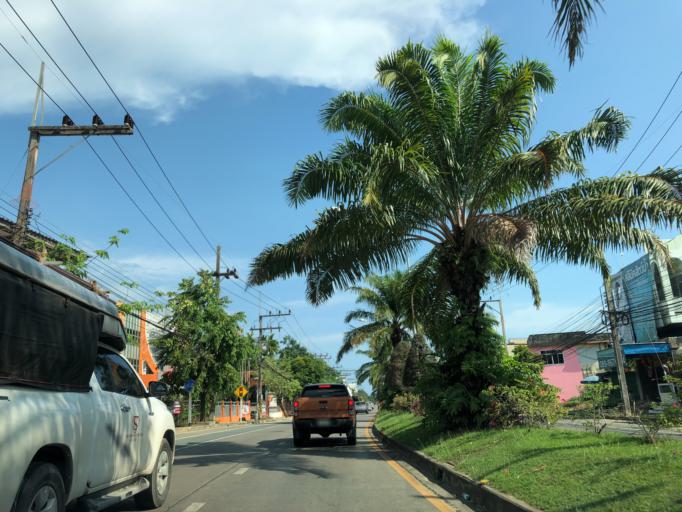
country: TH
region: Krabi
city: Krabi
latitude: 8.0820
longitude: 98.9148
